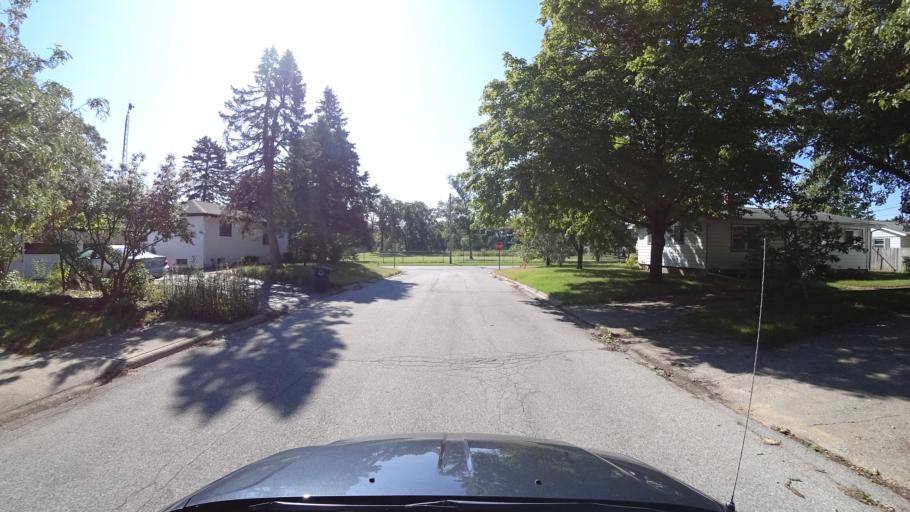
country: US
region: Indiana
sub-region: LaPorte County
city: Michigan City
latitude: 41.7027
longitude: -86.8784
